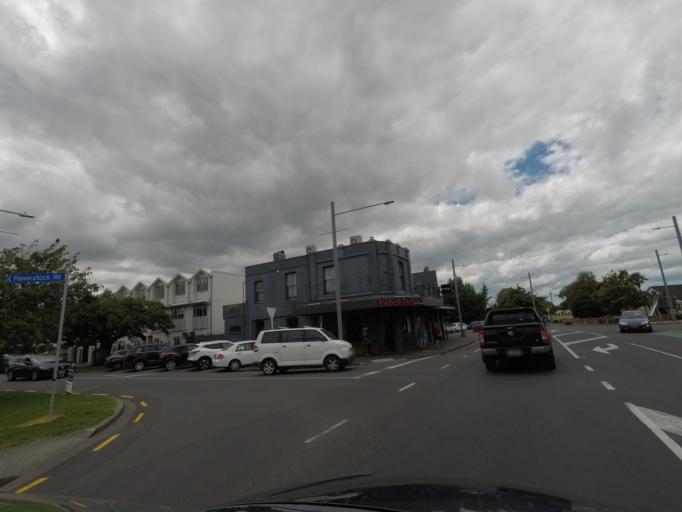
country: NZ
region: Auckland
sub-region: Auckland
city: Auckland
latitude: -36.8934
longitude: 174.7362
